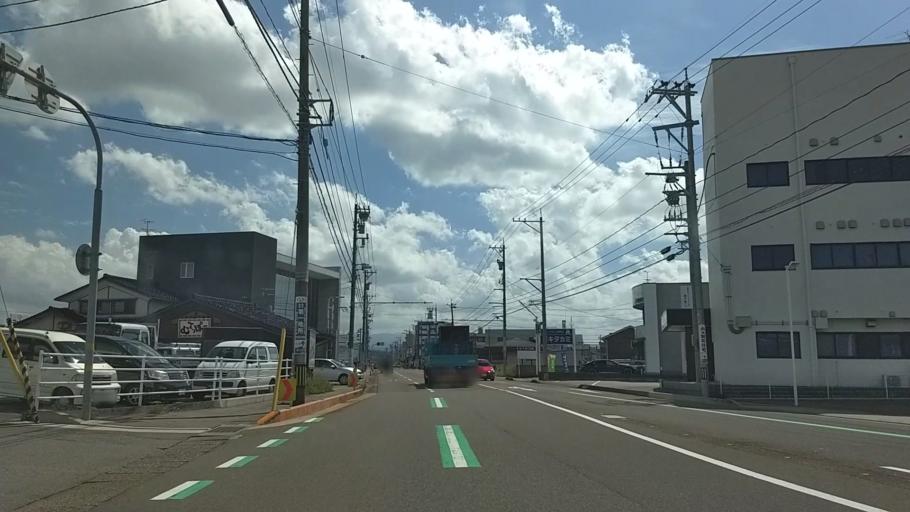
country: JP
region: Ishikawa
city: Kanazawa-shi
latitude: 36.6047
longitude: 136.6353
